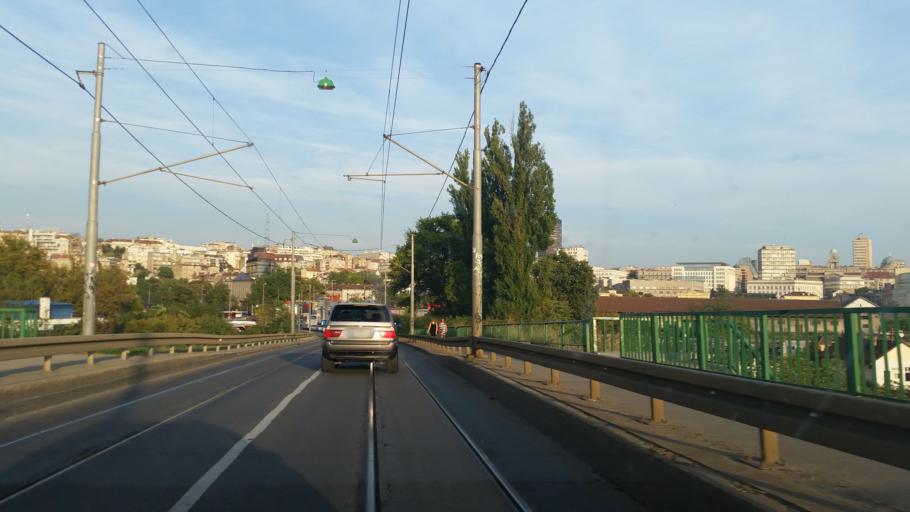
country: RS
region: Central Serbia
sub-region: Belgrade
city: Stari Grad
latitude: 44.8107
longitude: 20.4505
